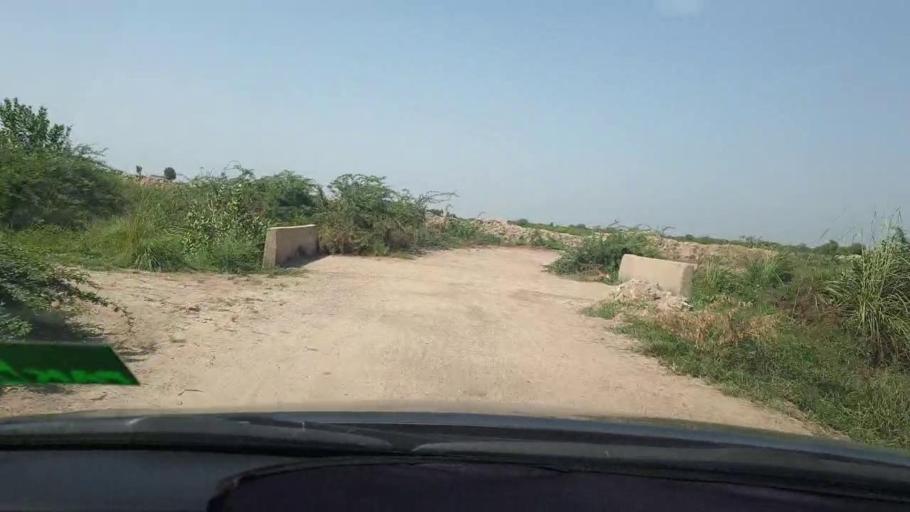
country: PK
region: Sindh
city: Digri
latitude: 24.9422
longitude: 69.1448
